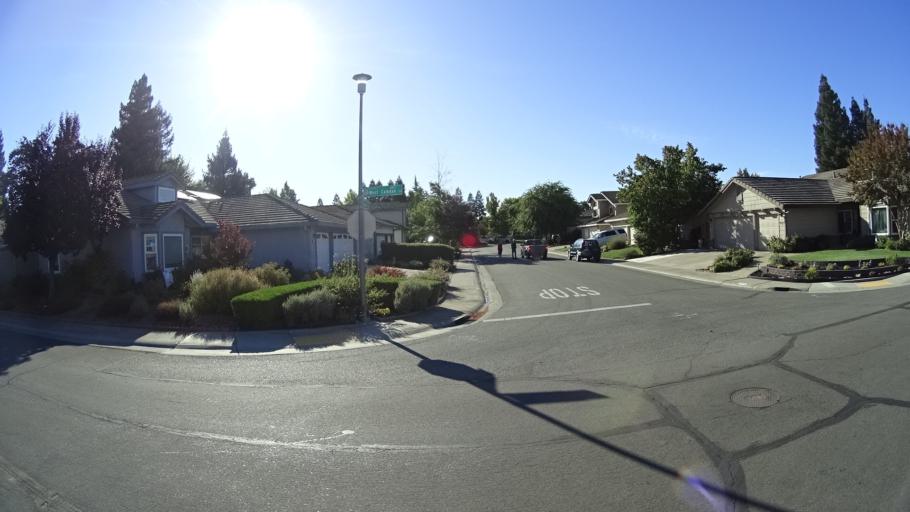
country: US
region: California
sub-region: Sacramento County
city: Elk Grove
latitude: 38.4315
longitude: -121.3794
